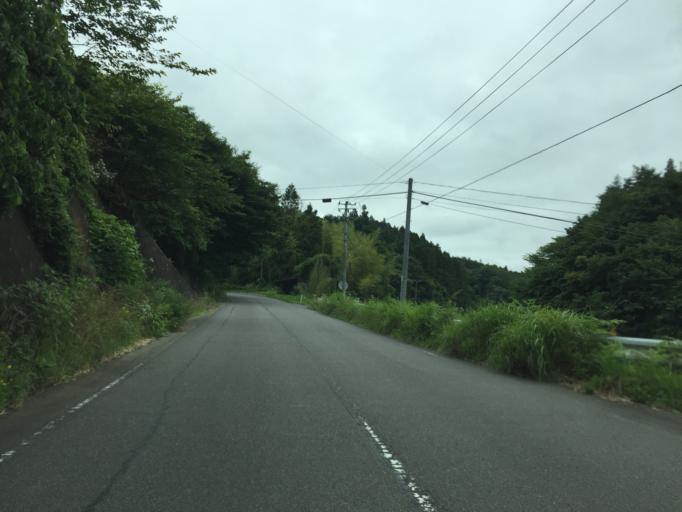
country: JP
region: Fukushima
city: Ishikawa
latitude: 37.1615
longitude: 140.5234
